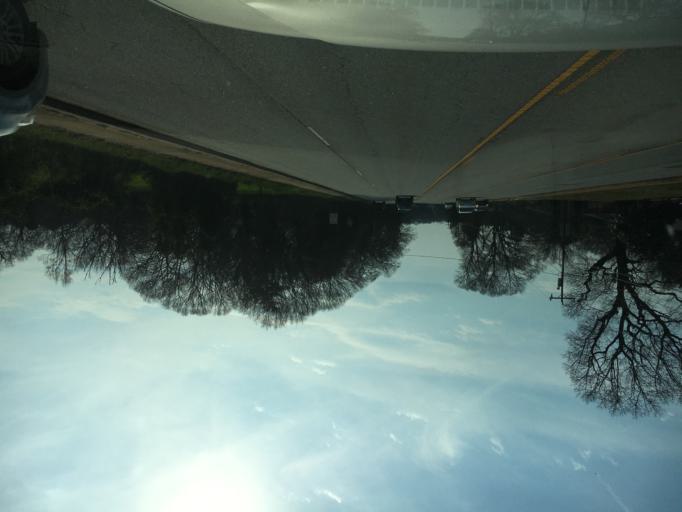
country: US
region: South Carolina
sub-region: Spartanburg County
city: Spartanburg
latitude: 34.9896
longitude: -81.9203
